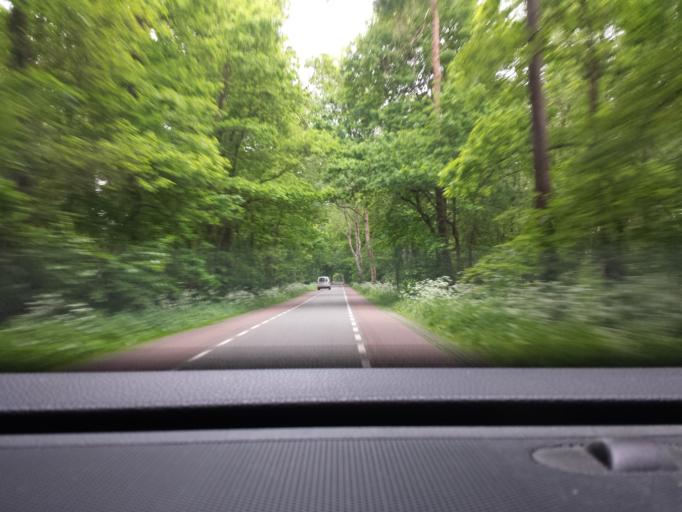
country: NL
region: Gelderland
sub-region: Gemeente Lochem
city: Lochem
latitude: 52.1174
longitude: 6.3628
